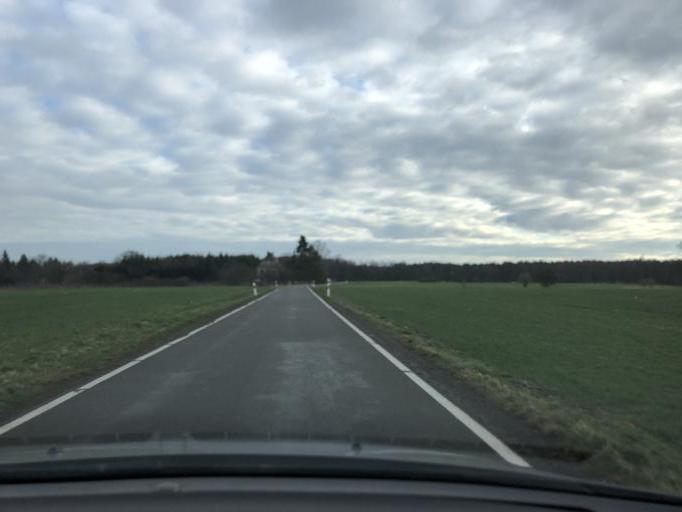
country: DE
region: Saxony
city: Grossbothen
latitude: 51.1836
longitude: 12.7938
